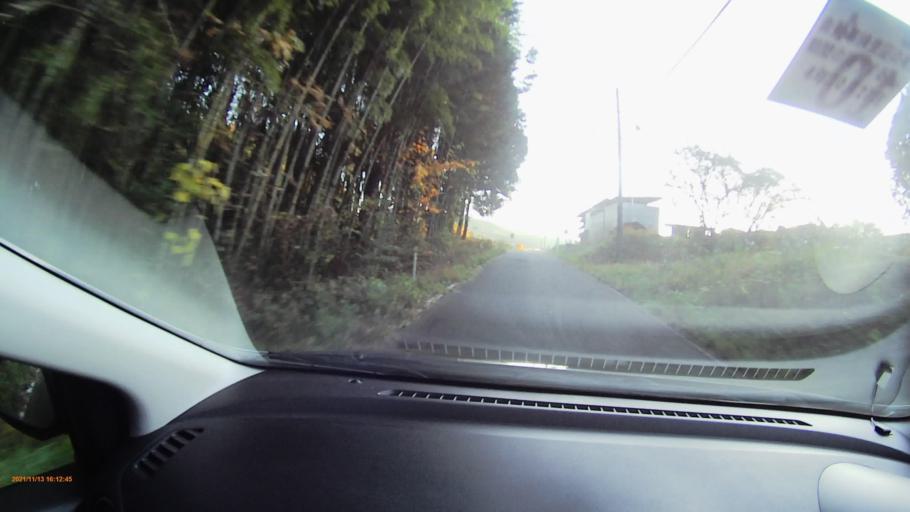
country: JP
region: Gifu
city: Nakatsugawa
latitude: 35.5808
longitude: 137.5119
